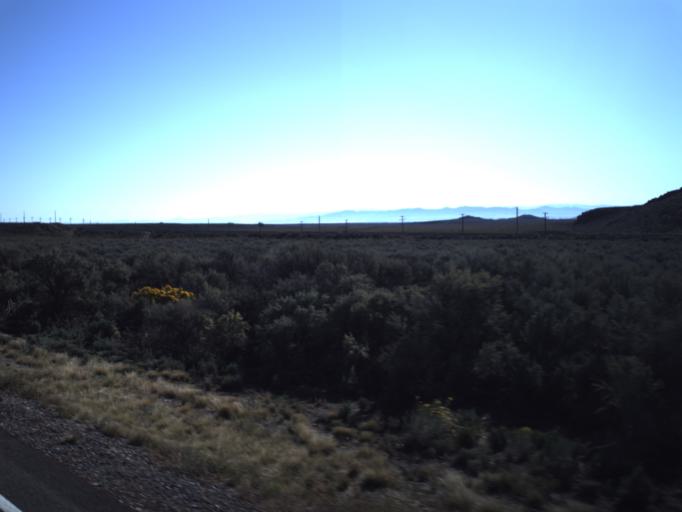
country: US
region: Utah
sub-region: Washington County
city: Enterprise
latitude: 37.7892
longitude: -113.9525
